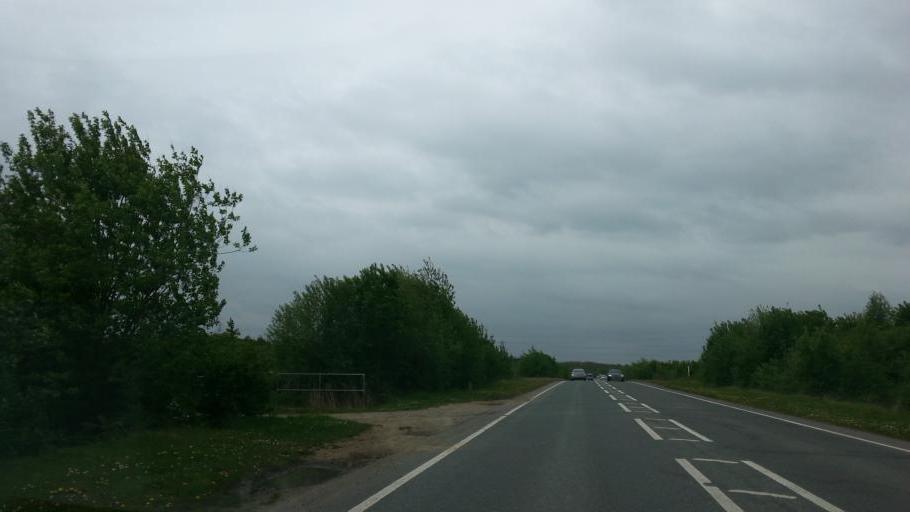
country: GB
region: England
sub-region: Lincolnshire
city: Bourne
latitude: 52.7593
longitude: -0.3939
